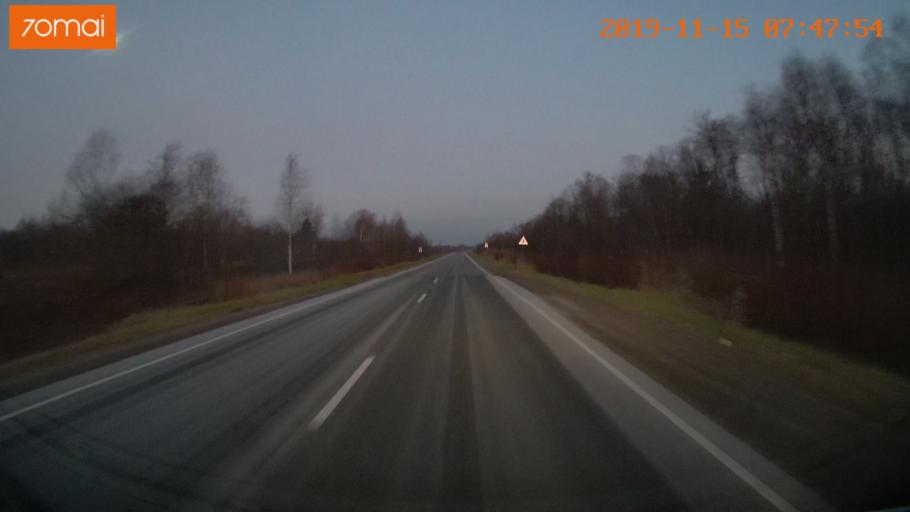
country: RU
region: Vologda
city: Sheksna
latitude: 58.8459
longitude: 38.2526
